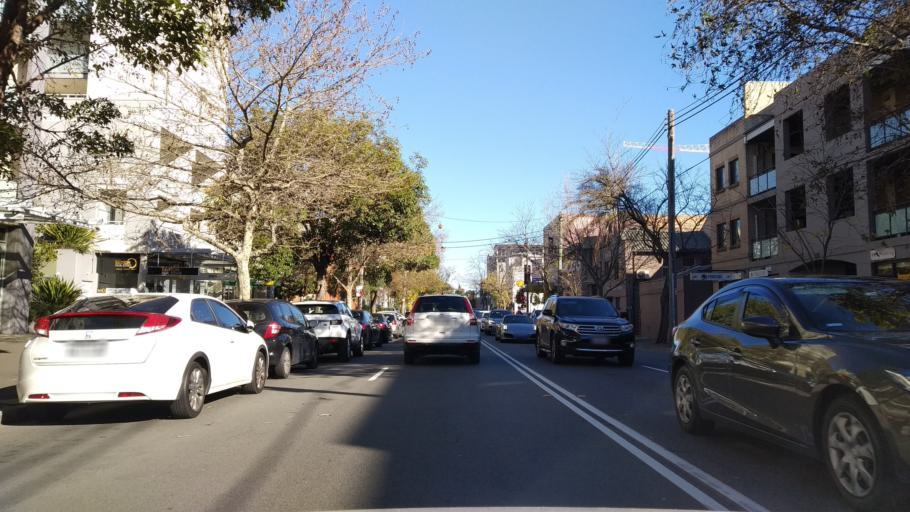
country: AU
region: New South Wales
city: Alexandria
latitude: -33.9156
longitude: 151.2007
